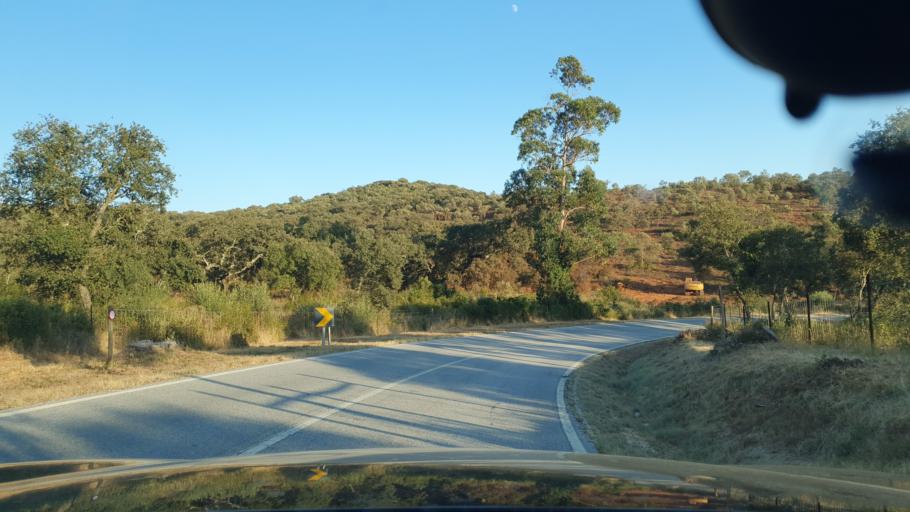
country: PT
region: Evora
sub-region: Estremoz
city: Estremoz
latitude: 38.9104
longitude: -7.6622
